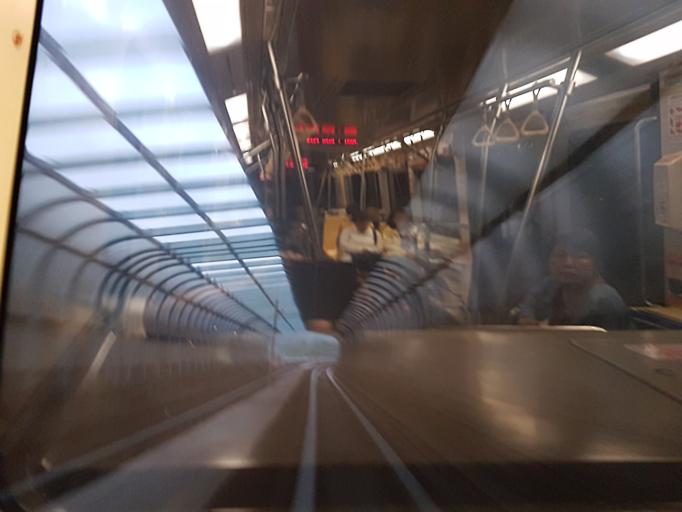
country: TW
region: Taipei
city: Taipei
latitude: 25.0761
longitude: 121.6071
